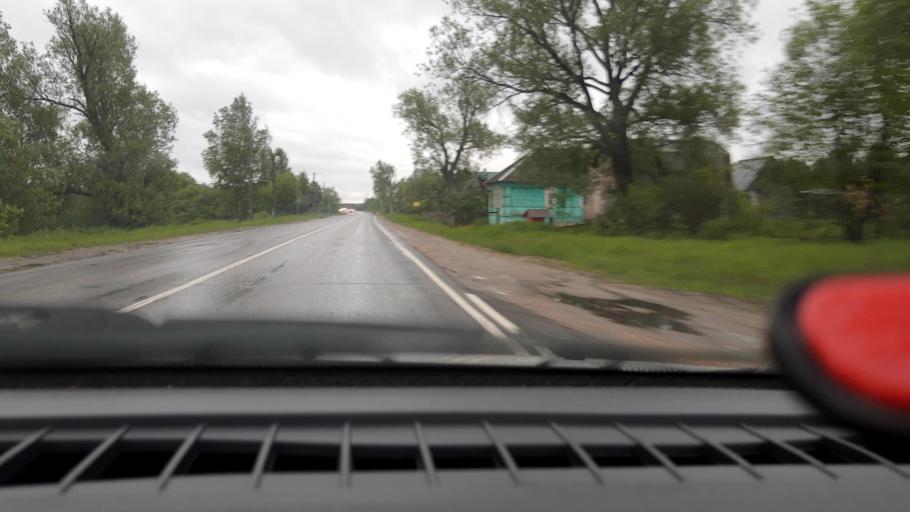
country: RU
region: Nizjnij Novgorod
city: Krasnyye Baki
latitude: 57.0118
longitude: 45.1132
